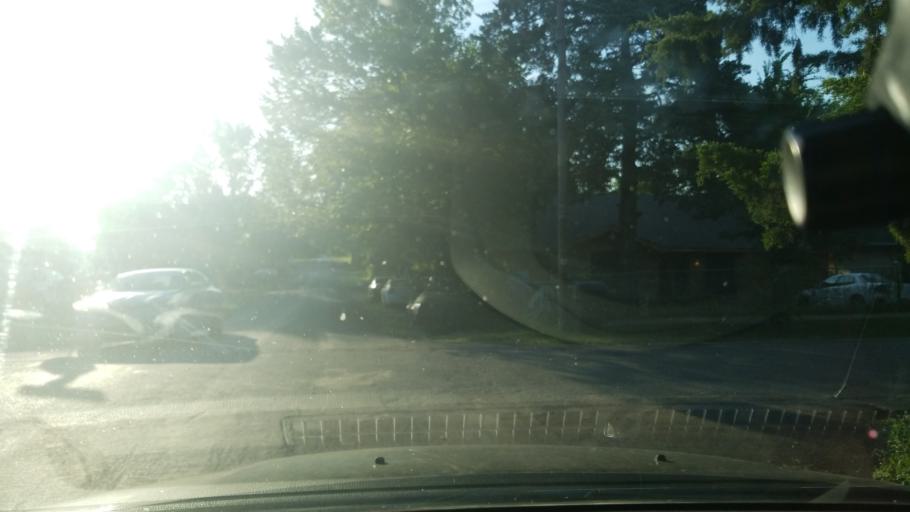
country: US
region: Texas
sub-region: Dallas County
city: Dallas
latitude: 32.7179
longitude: -96.8207
